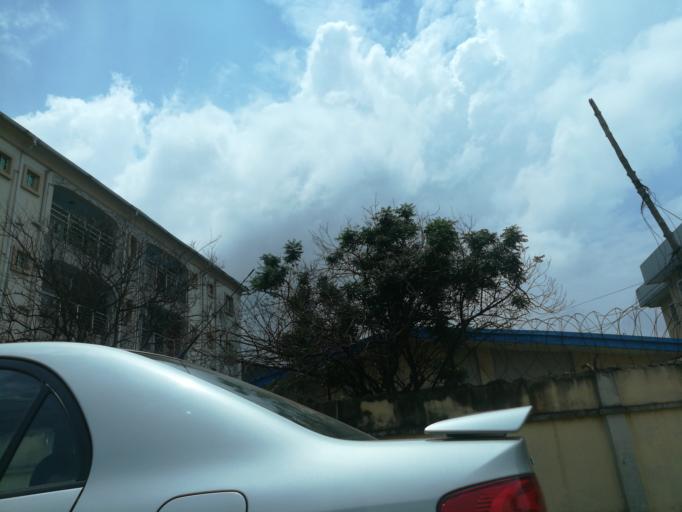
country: NG
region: Lagos
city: Oshodi
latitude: 6.5483
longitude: 3.3294
